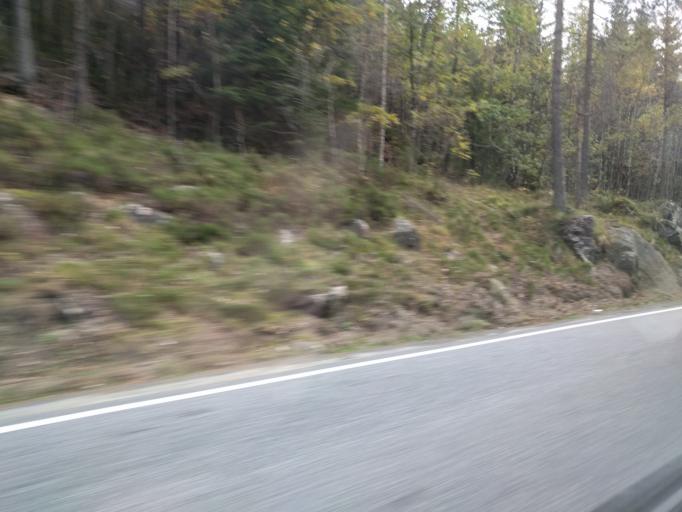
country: NO
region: Vest-Agder
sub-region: Songdalen
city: Nodeland
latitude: 58.2985
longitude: 7.8268
